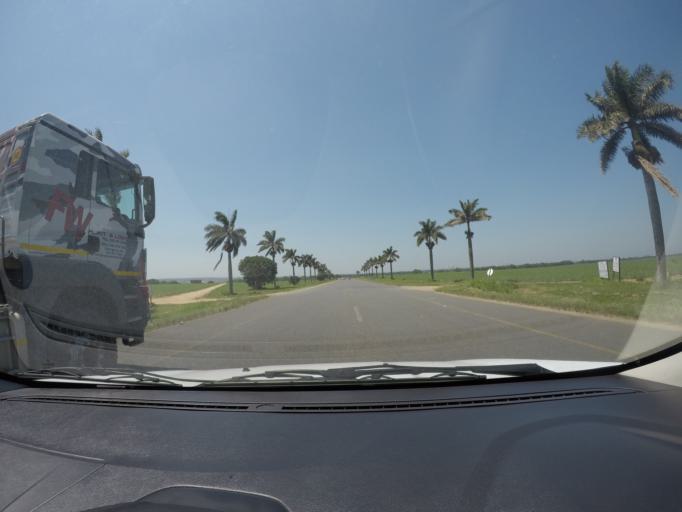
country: ZA
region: KwaZulu-Natal
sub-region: uThungulu District Municipality
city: Empangeni
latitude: -28.8074
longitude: 31.9570
